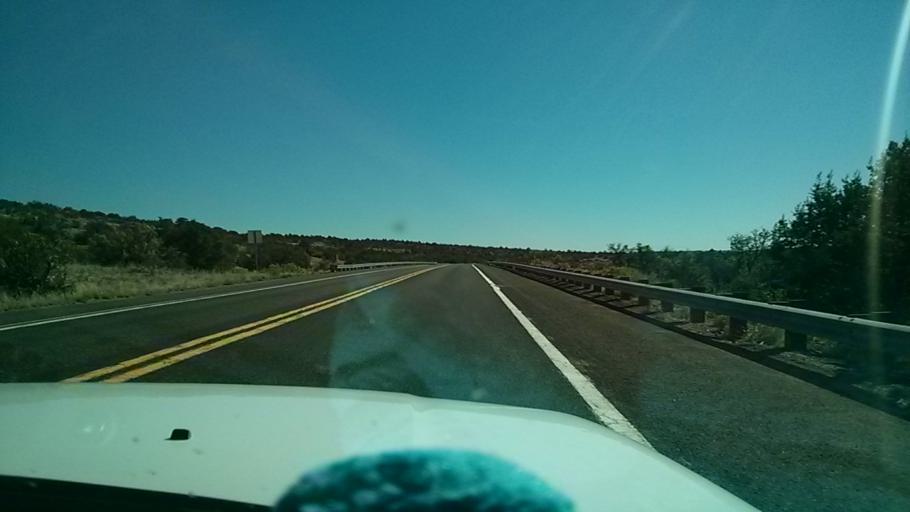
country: US
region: Arizona
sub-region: Mohave County
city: Peach Springs
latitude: 35.5485
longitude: -113.3954
